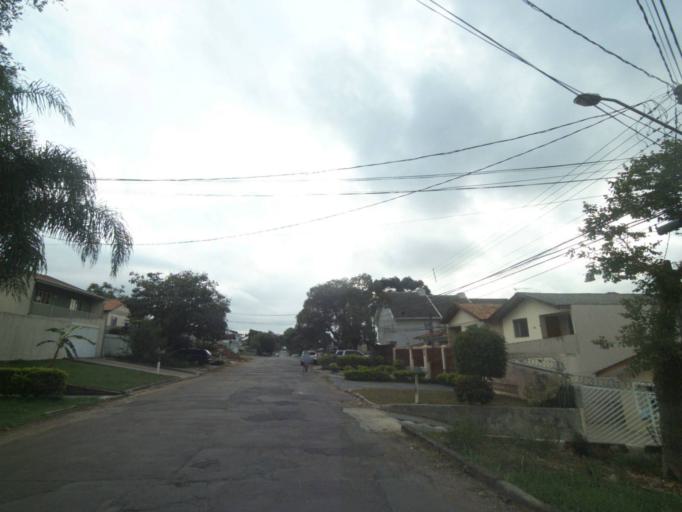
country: BR
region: Parana
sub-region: Pinhais
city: Pinhais
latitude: -25.4128
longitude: -49.2118
